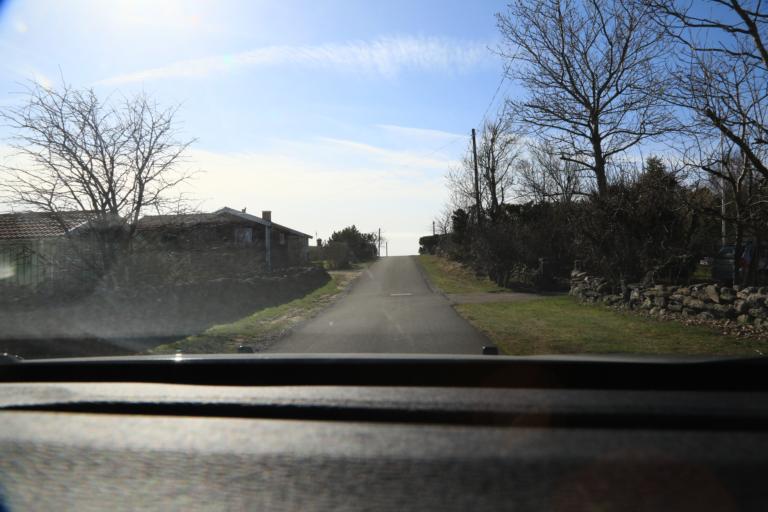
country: SE
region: Halland
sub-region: Varbergs Kommun
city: Varberg
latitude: 57.1233
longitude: 12.2059
